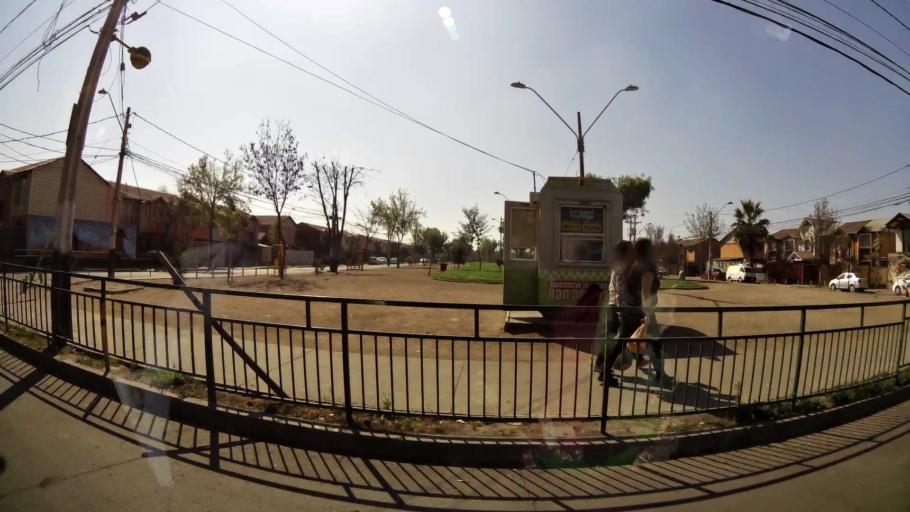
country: CL
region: Santiago Metropolitan
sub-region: Provincia de Santiago
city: Lo Prado
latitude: -33.3593
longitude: -70.7427
